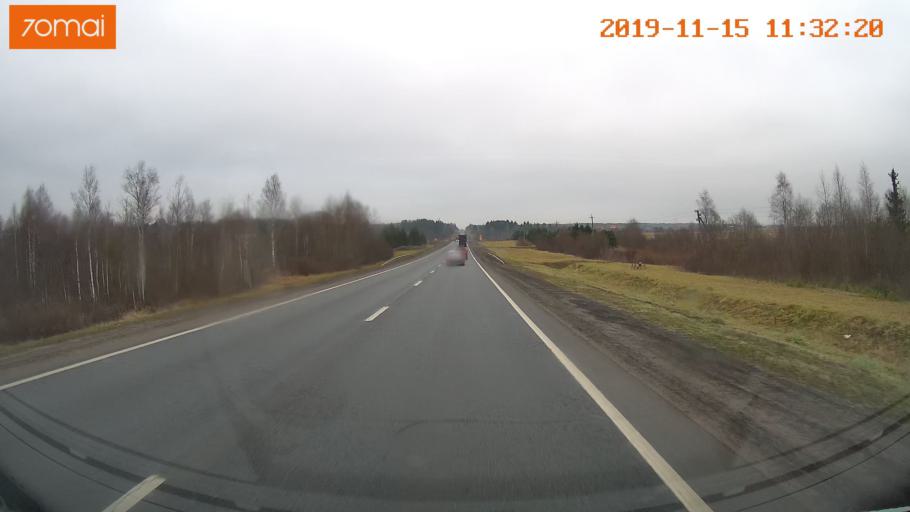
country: RU
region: Vologda
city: Molochnoye
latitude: 59.1850
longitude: 39.5716
